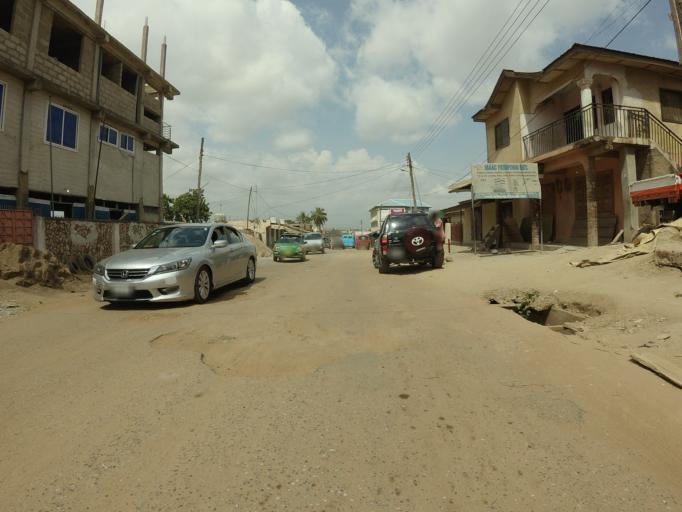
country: GH
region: Greater Accra
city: Dome
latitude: 5.6099
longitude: -0.2456
